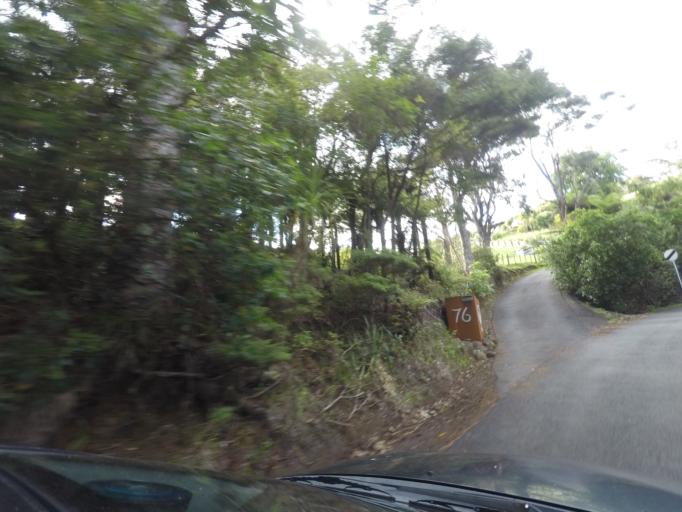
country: NZ
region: Auckland
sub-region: Auckland
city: Titirangi
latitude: -37.0192
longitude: 174.5510
